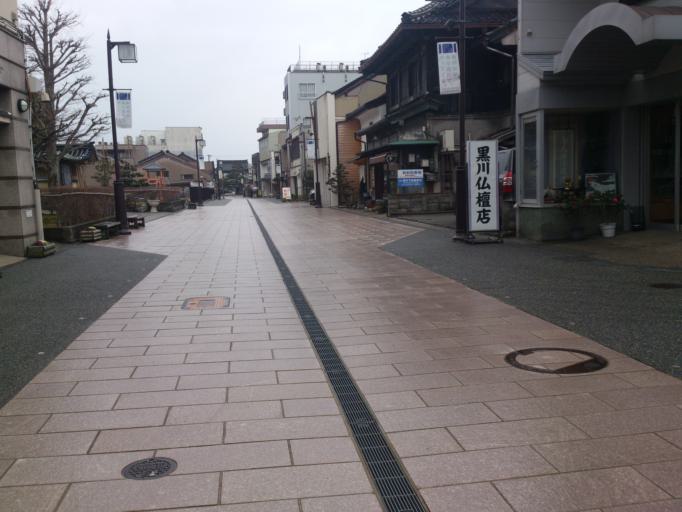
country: JP
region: Ishikawa
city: Kanazawa-shi
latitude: 36.5745
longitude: 136.6556
